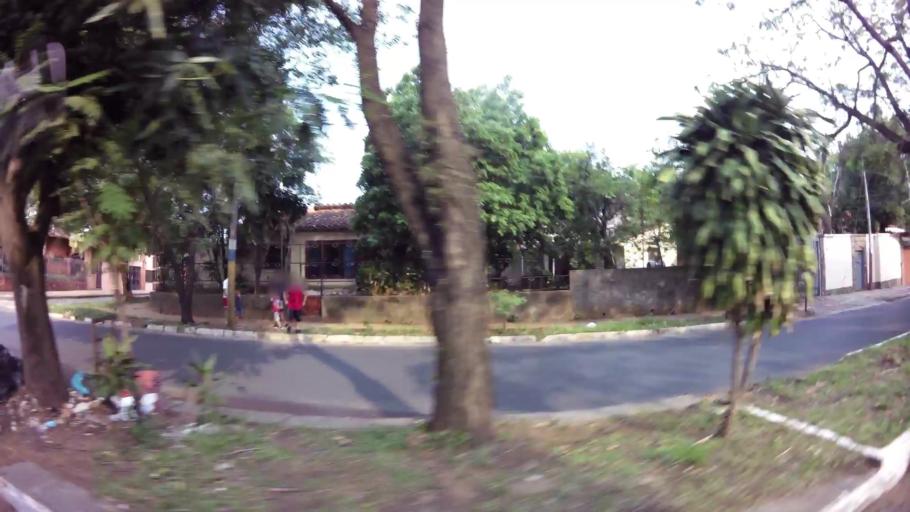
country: PY
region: Asuncion
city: Asuncion
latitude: -25.3098
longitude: -57.6099
